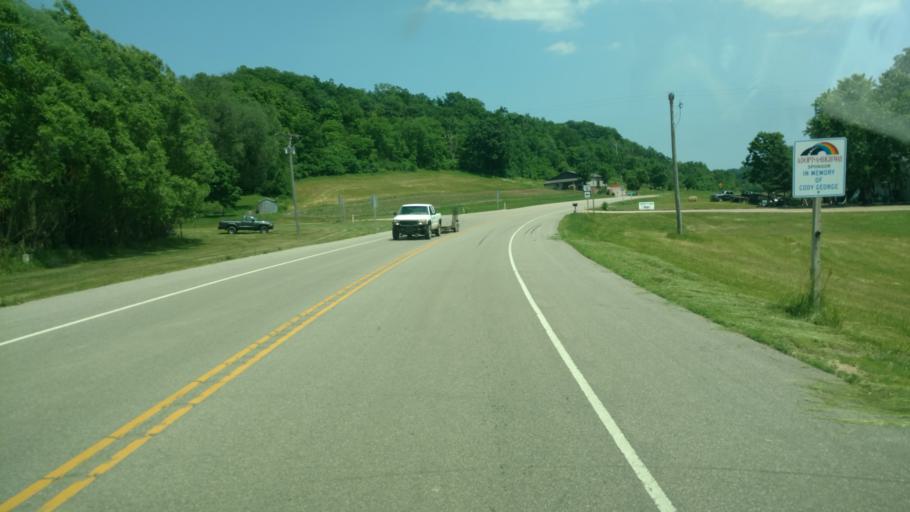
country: US
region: Wisconsin
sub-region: Vernon County
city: Viroqua
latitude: 43.4691
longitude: -90.7335
